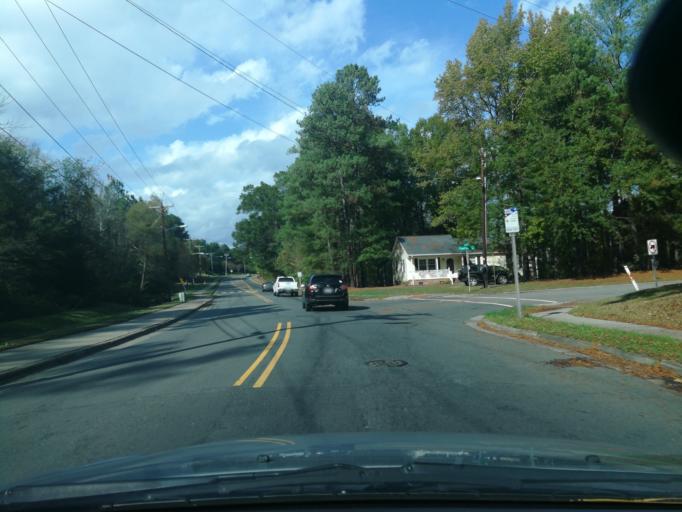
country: US
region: North Carolina
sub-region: Durham County
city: Durham
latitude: 36.0440
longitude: -78.9353
